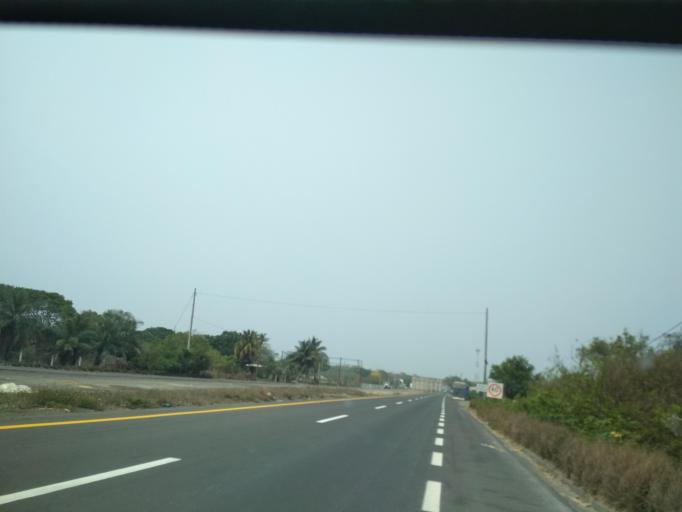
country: MX
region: Veracruz
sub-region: Veracruz
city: Delfino Victoria (Santa Fe)
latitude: 19.1996
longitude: -96.2711
